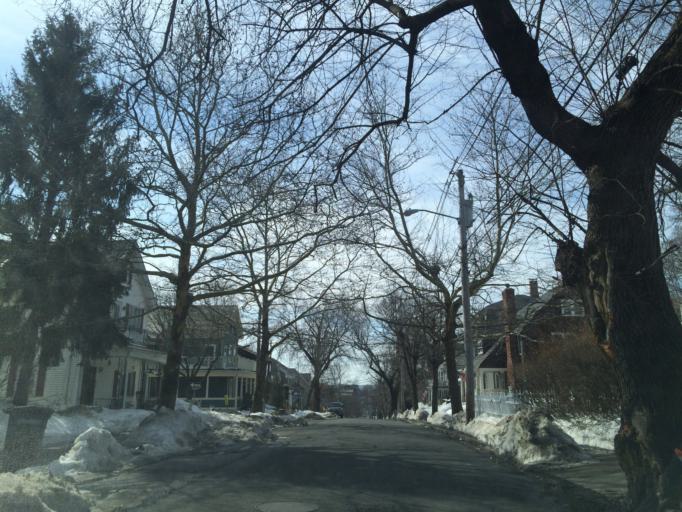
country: US
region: Massachusetts
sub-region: Middlesex County
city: Somerville
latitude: 42.3944
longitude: -71.0993
